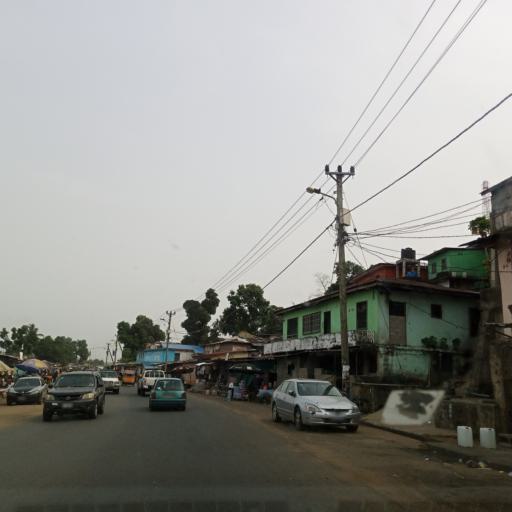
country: LR
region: Montserrado
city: Monrovia
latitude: 6.3040
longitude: -10.7947
